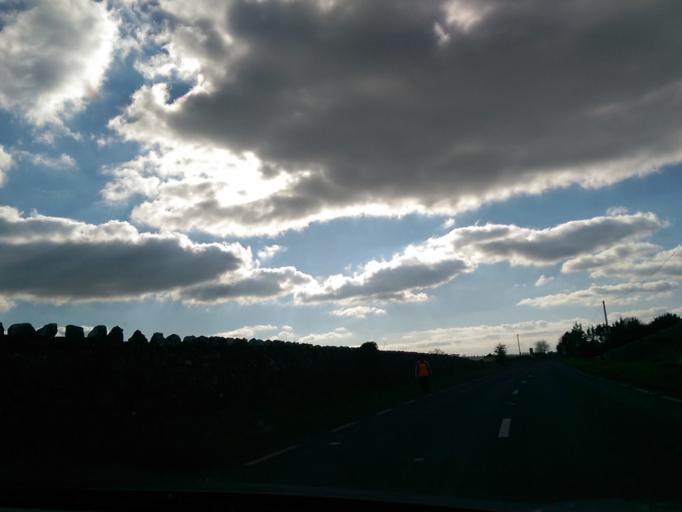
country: IE
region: Connaught
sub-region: County Galway
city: Loughrea
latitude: 53.1991
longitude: -8.4451
